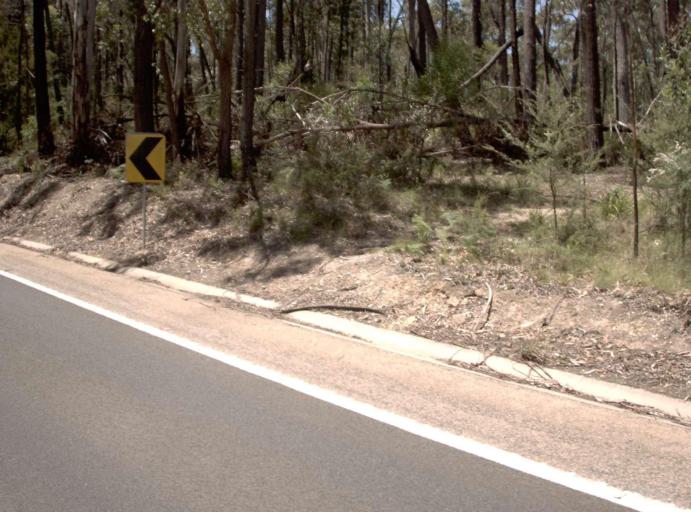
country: AU
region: Victoria
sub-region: East Gippsland
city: Lakes Entrance
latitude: -37.7055
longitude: 148.5765
